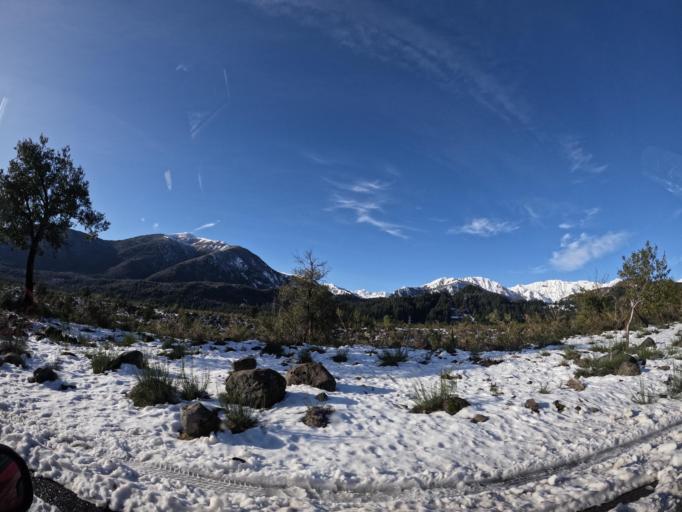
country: CL
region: Biobio
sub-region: Provincia de Nuble
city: Coihueco
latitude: -37.3683
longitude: -71.5007
